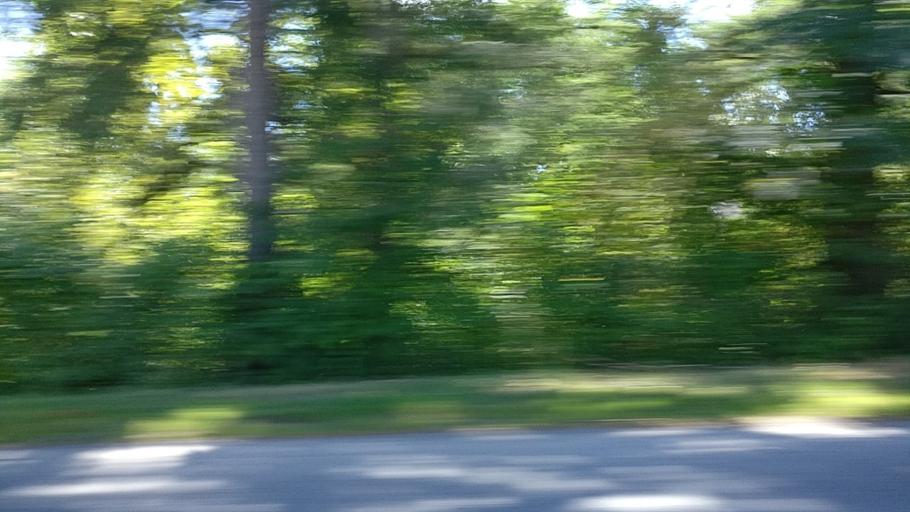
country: US
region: Washington
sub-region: Whatcom County
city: Blaine
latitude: 49.0167
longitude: -122.7225
